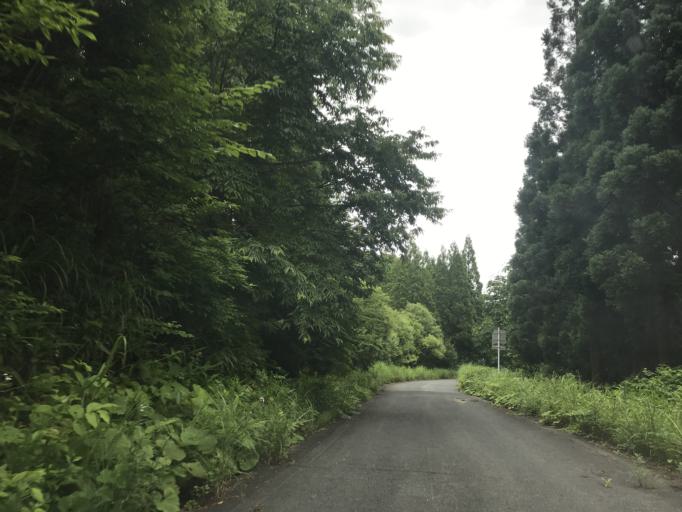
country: JP
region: Iwate
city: Ichinoseki
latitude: 38.9540
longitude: 140.8789
